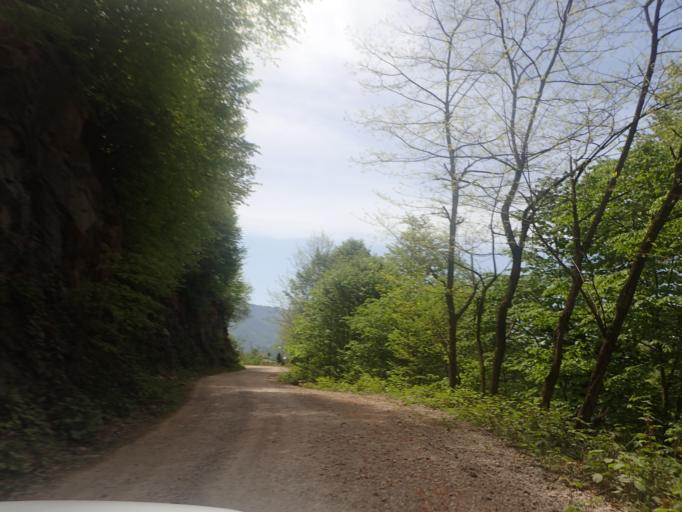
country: TR
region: Ordu
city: Kabaduz
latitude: 40.8000
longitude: 37.8854
